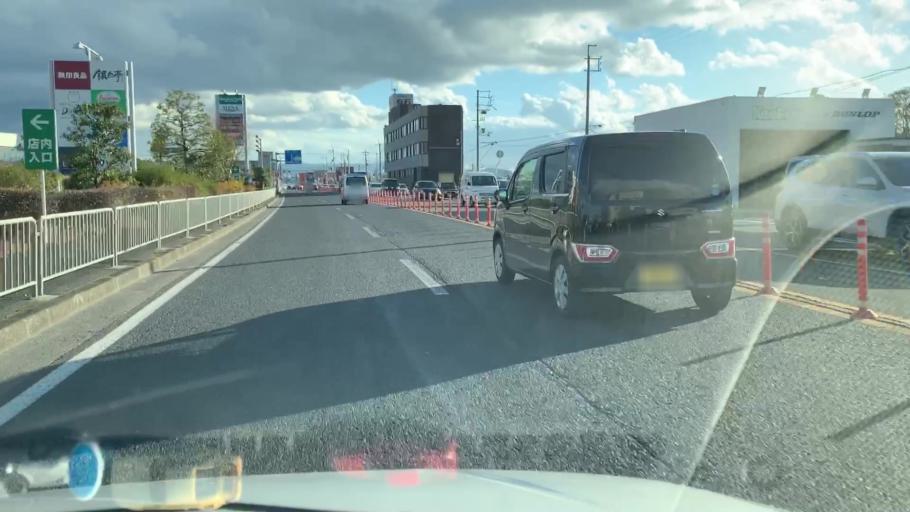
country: JP
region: Wakayama
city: Wakayama-shi
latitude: 34.2394
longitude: 135.1521
